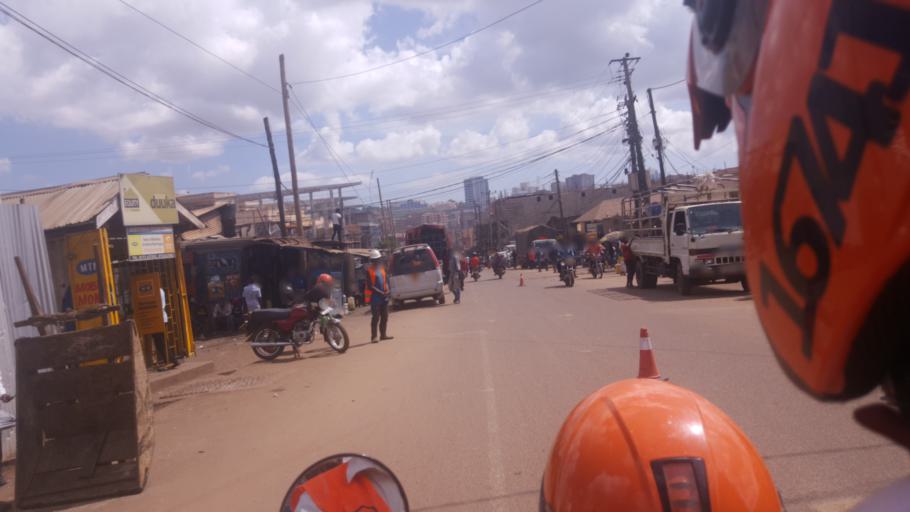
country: UG
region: Central Region
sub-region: Kampala District
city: Kampala
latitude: 0.3088
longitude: 32.5702
